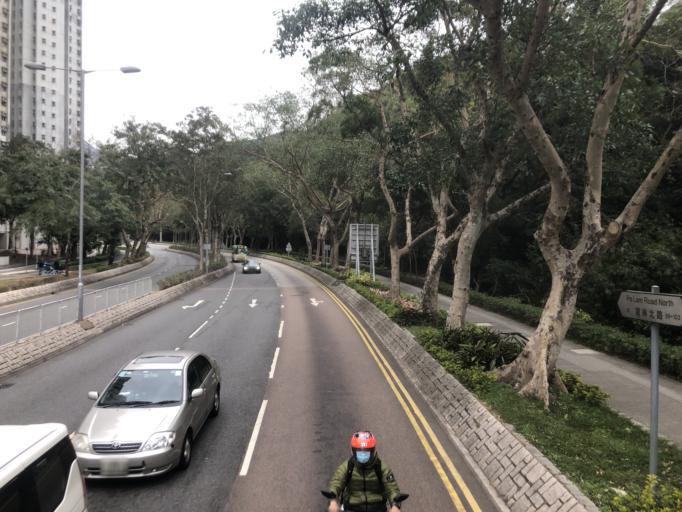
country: HK
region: Sai Kung
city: Sai Kung
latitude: 22.3262
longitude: 114.2584
